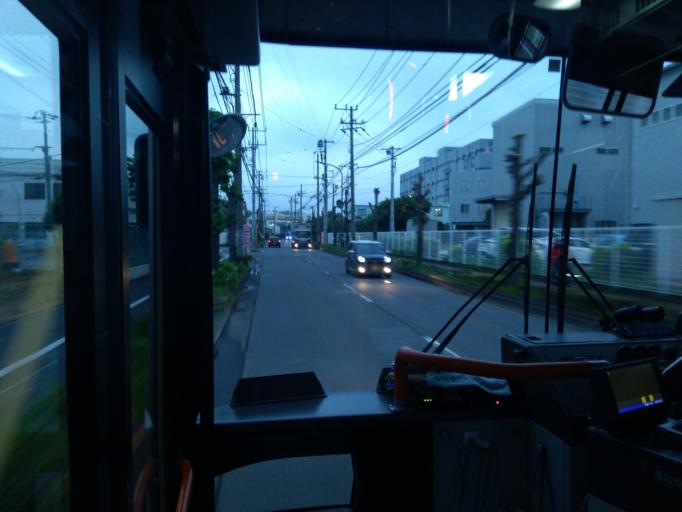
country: JP
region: Kanagawa
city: Hiratsuka
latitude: 35.3405
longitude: 139.3605
